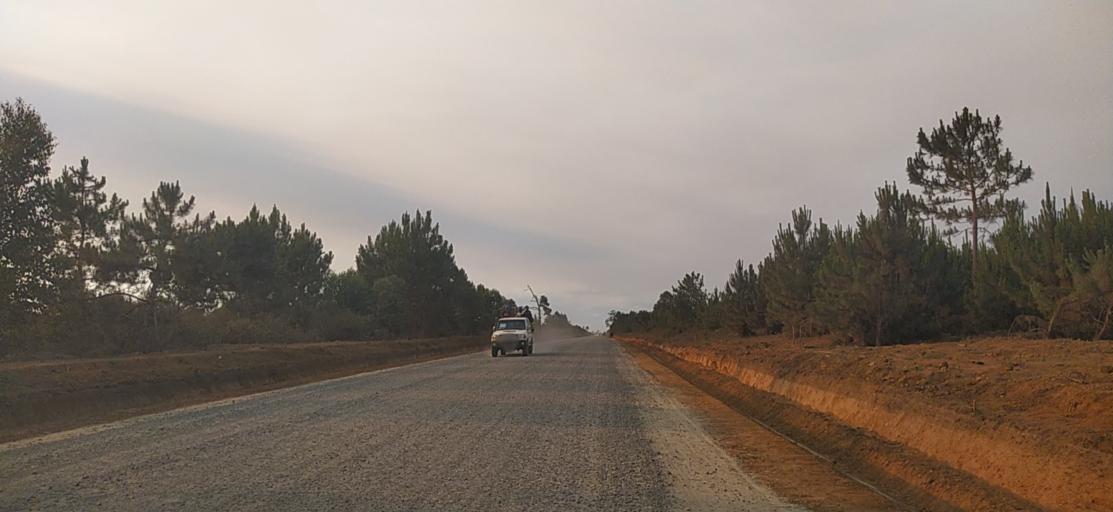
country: MG
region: Alaotra Mangoro
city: Moramanga
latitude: -18.5437
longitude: 48.2599
